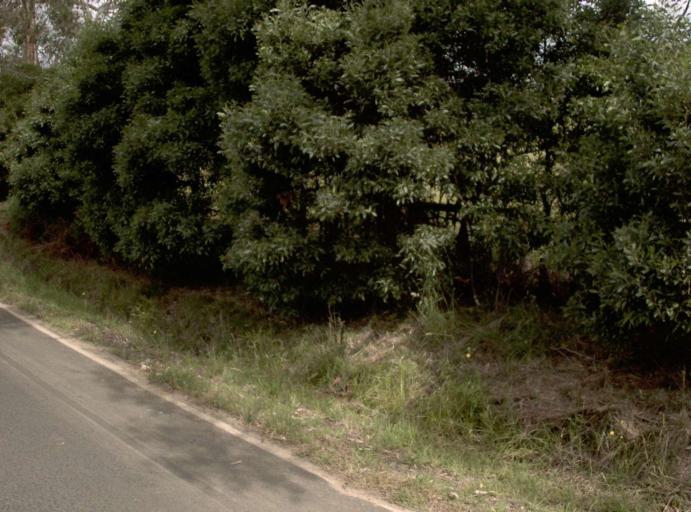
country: AU
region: Victoria
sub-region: Latrobe
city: Traralgon
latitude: -38.3780
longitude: 146.7787
